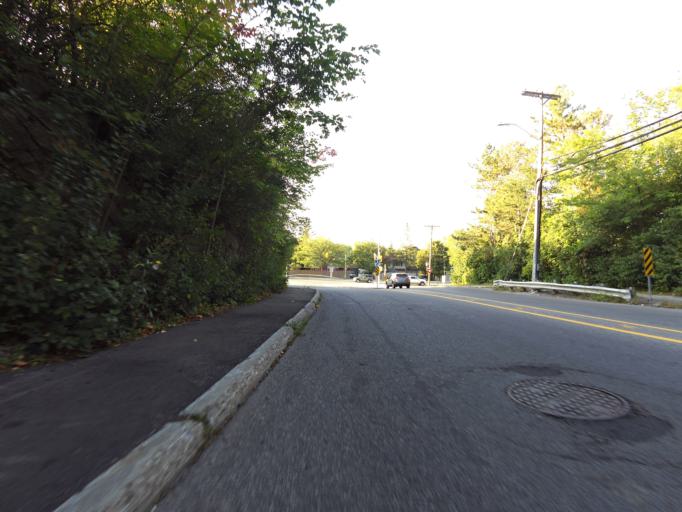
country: CA
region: Ontario
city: Ottawa
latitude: 45.3641
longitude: -75.6769
